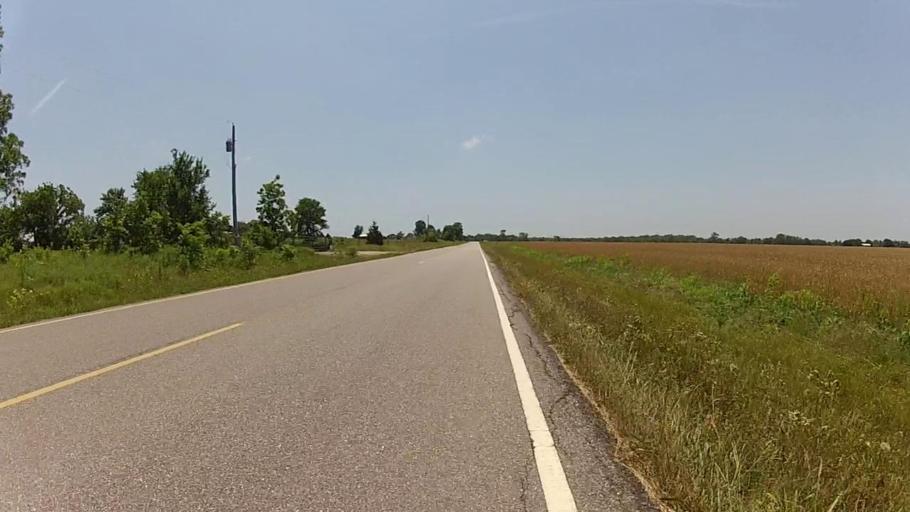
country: US
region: Kansas
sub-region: Montgomery County
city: Cherryvale
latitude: 37.1999
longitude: -95.5391
